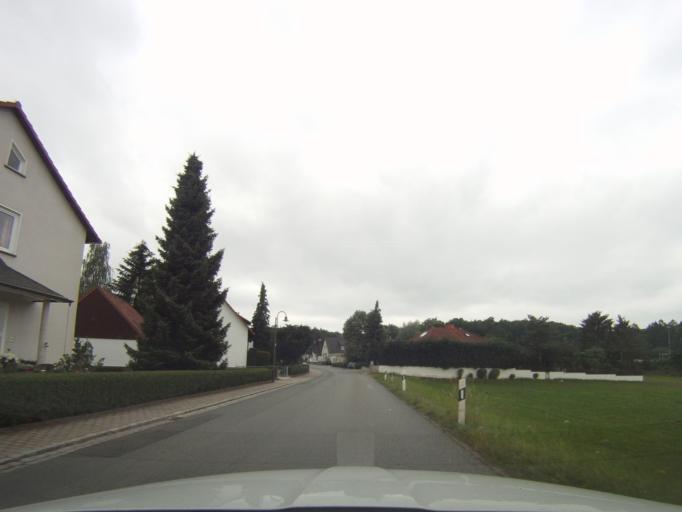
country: DE
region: Bavaria
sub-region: Upper Franconia
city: Weitramsdorf
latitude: 50.2263
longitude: 10.9113
